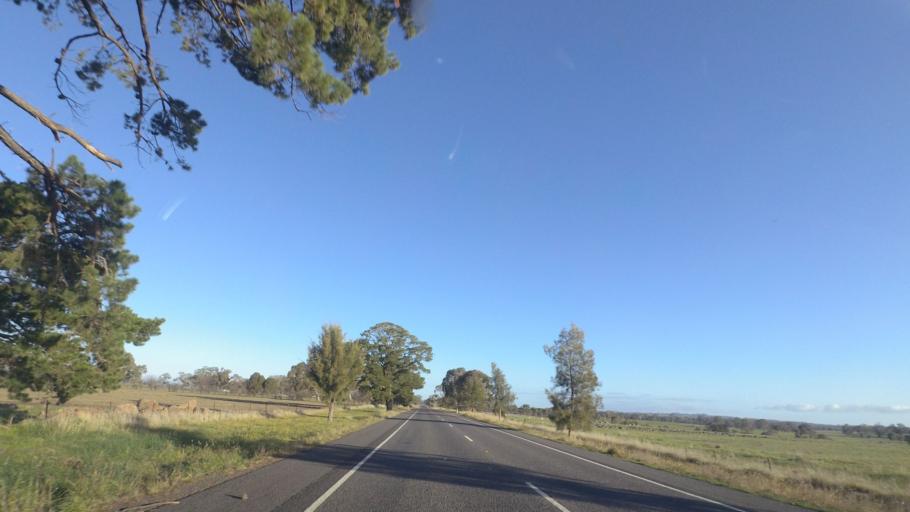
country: AU
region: Victoria
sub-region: Mount Alexander
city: Castlemaine
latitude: -37.0395
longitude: 144.5286
